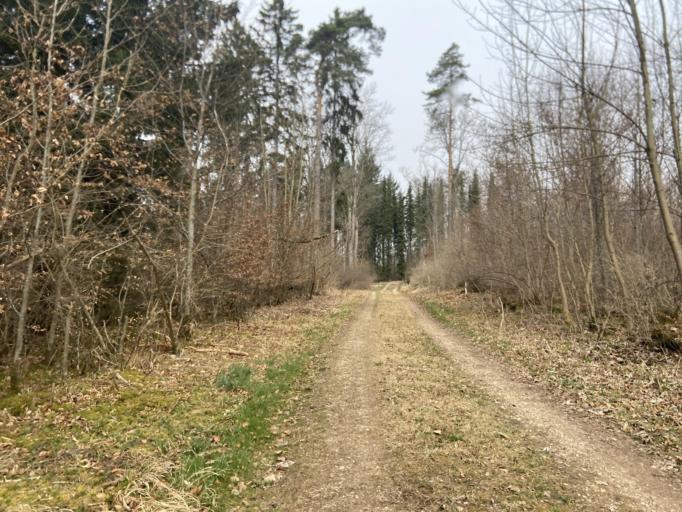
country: DE
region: Baden-Wuerttemberg
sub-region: Tuebingen Region
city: Sigmaringen
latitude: 48.1067
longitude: 9.2474
